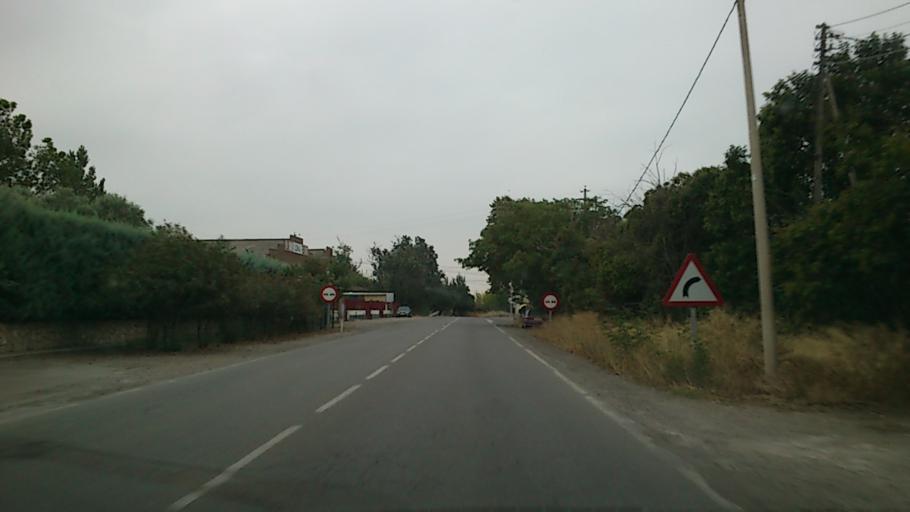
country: ES
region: Aragon
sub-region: Provincia de Zaragoza
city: Villanueva de Gallego
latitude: 41.7010
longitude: -0.8152
